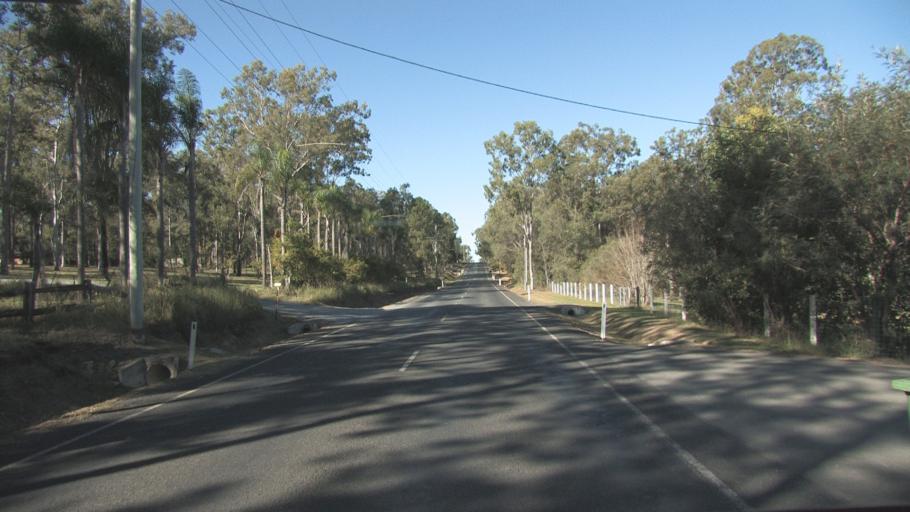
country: AU
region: Queensland
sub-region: Logan
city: Park Ridge South
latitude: -27.7227
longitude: 153.0022
